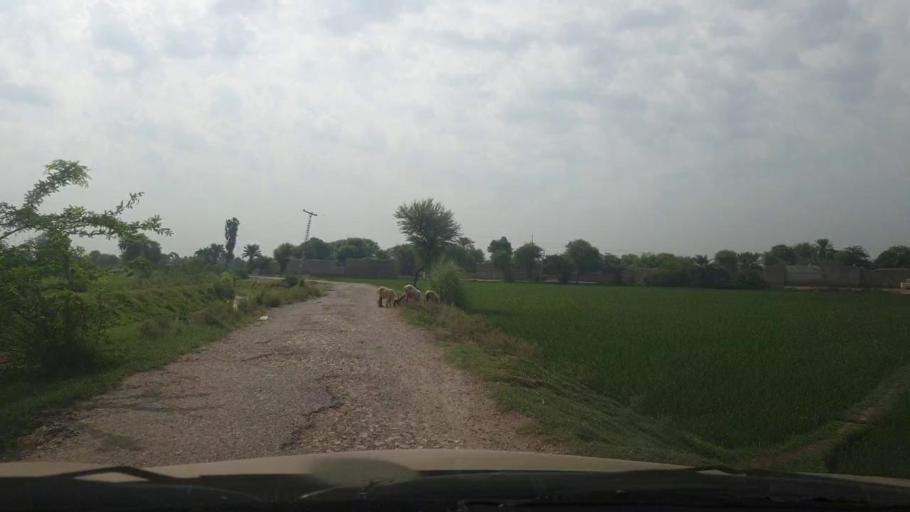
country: PK
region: Sindh
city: Larkana
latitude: 27.6389
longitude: 68.2053
